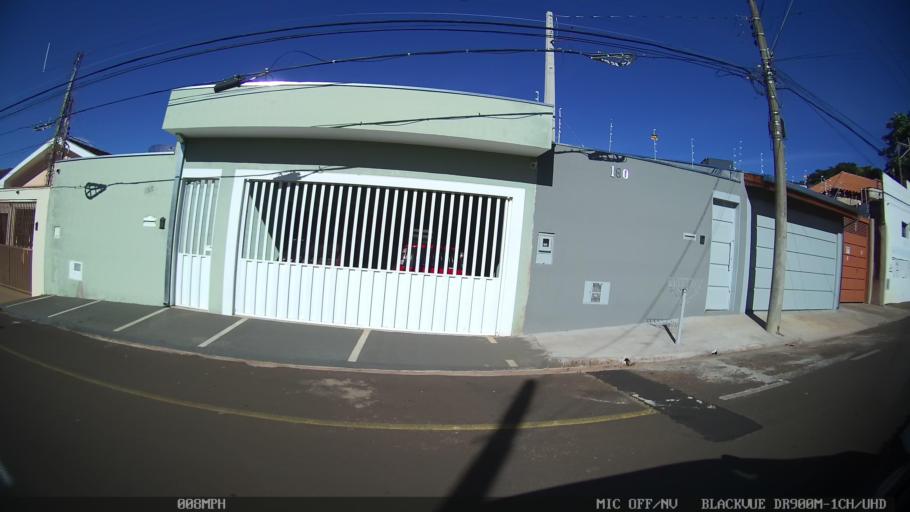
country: BR
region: Sao Paulo
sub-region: Franca
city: Franca
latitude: -20.5290
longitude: -47.4116
